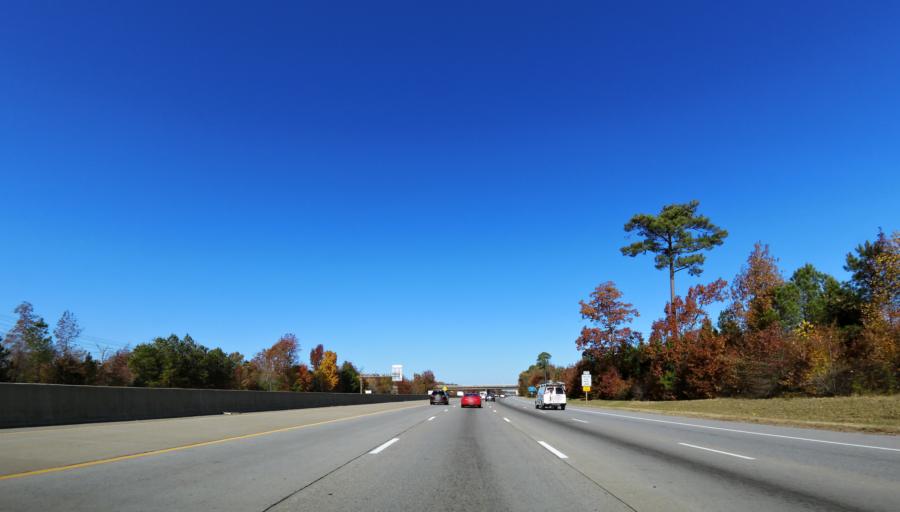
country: US
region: Virginia
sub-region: York County
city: Yorktown
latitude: 37.1222
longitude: -76.5153
